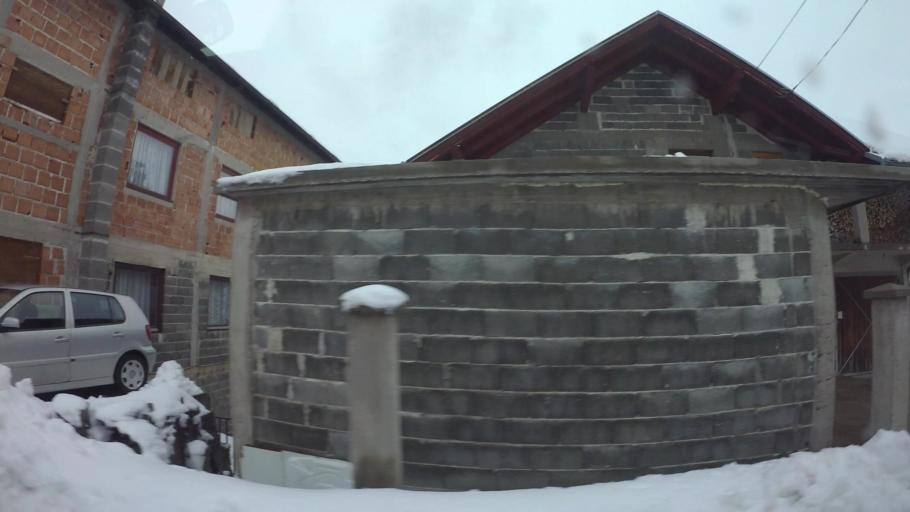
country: BA
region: Federation of Bosnia and Herzegovina
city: Hadzici
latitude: 43.8489
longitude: 18.2714
